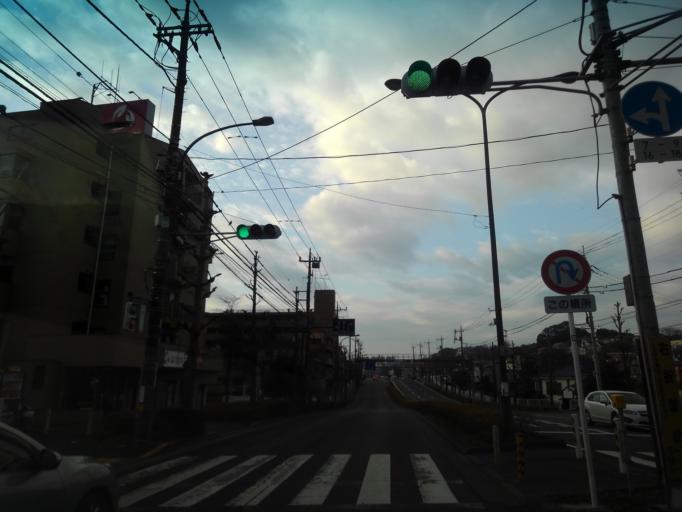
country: JP
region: Tokyo
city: Hino
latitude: 35.6471
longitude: 139.4530
